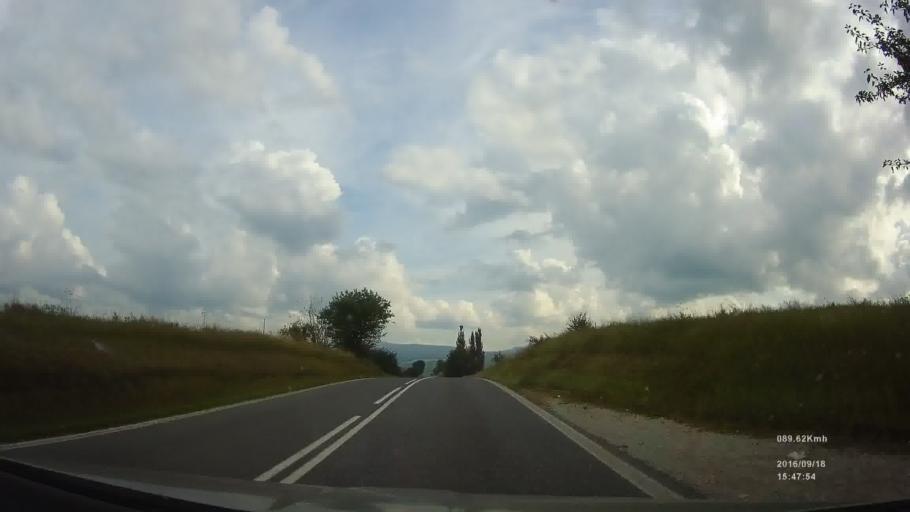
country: SK
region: Kosicky
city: Spisska Nova Ves
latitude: 48.9320
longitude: 20.5918
